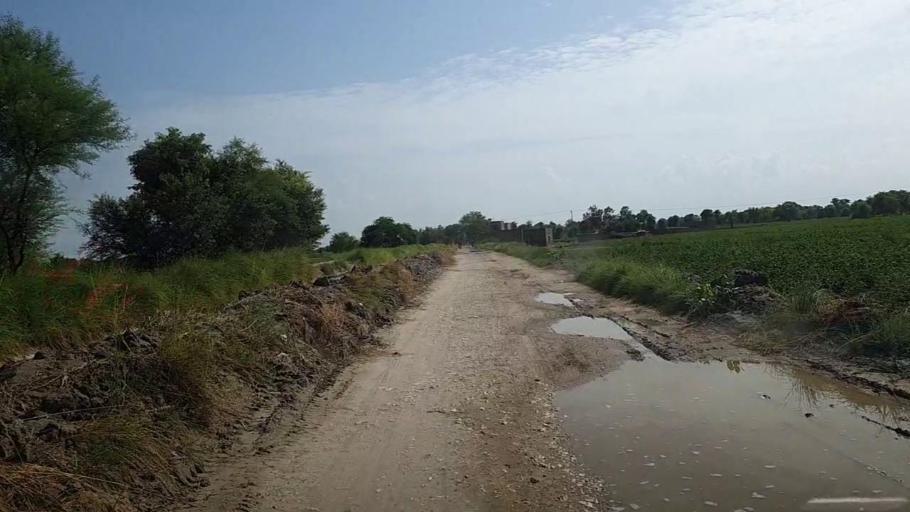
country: PK
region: Sindh
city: Bhiria
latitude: 26.8804
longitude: 68.2319
